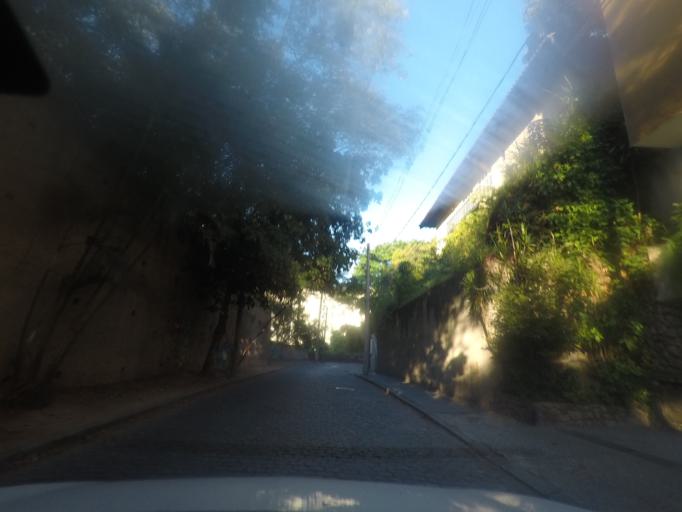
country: BR
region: Rio de Janeiro
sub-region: Rio De Janeiro
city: Rio de Janeiro
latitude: -22.9301
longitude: -43.1854
